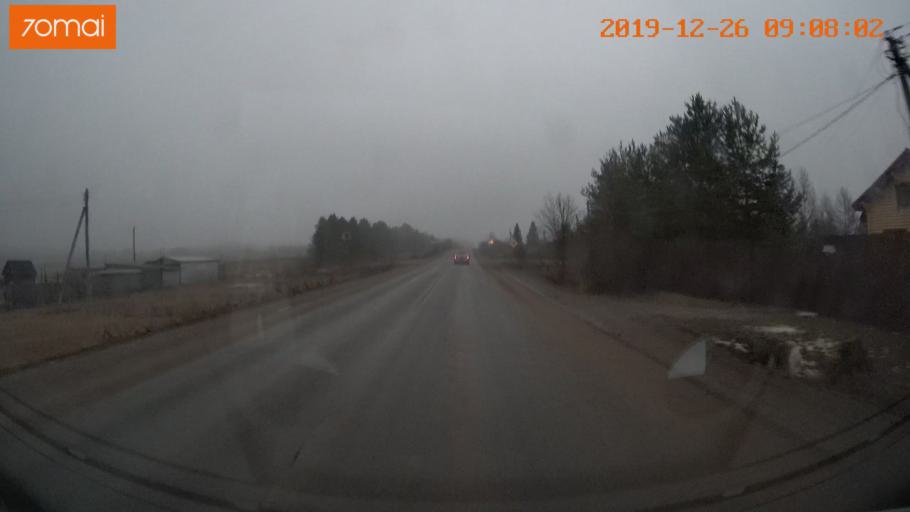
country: RU
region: Vologda
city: Gryazovets
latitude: 58.8524
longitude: 40.2473
